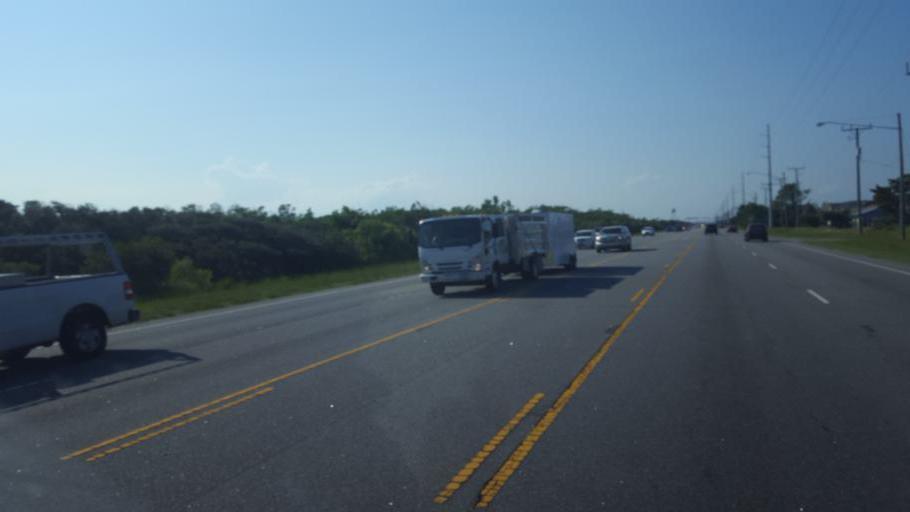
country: US
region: North Carolina
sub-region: Dare County
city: Kill Devil Hills
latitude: 36.0154
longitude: -75.6619
